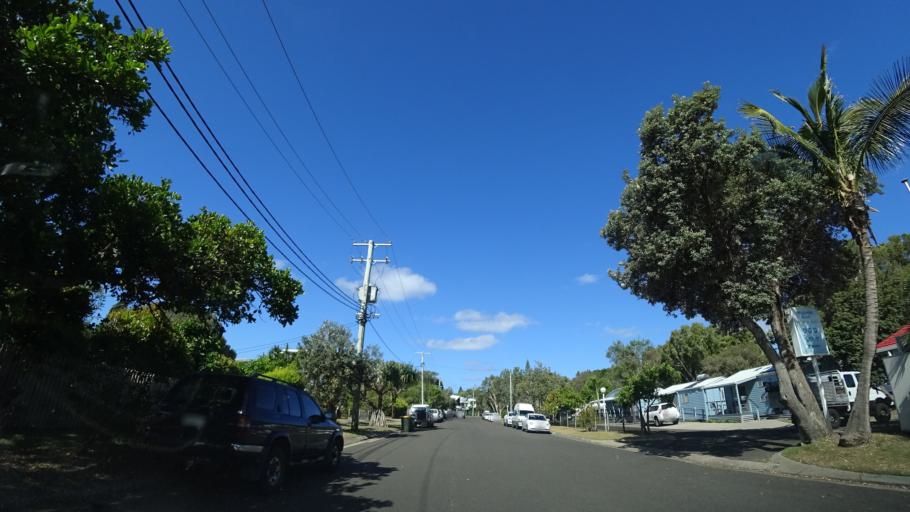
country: AU
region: Queensland
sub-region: Sunshine Coast
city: Mooloolaba
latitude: -26.6172
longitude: 153.0989
